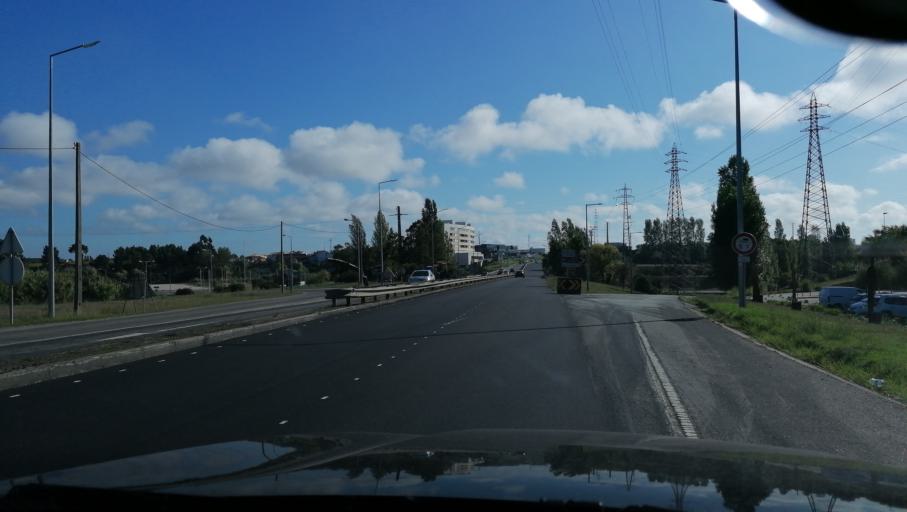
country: PT
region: Aveiro
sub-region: Aveiro
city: Aveiro
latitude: 40.6377
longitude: -8.6343
